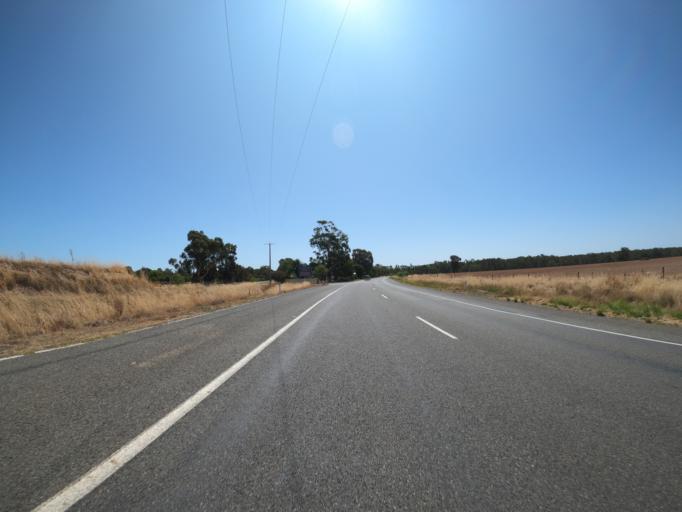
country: AU
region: New South Wales
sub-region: Corowa Shire
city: Corowa
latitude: -36.0701
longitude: 146.2090
